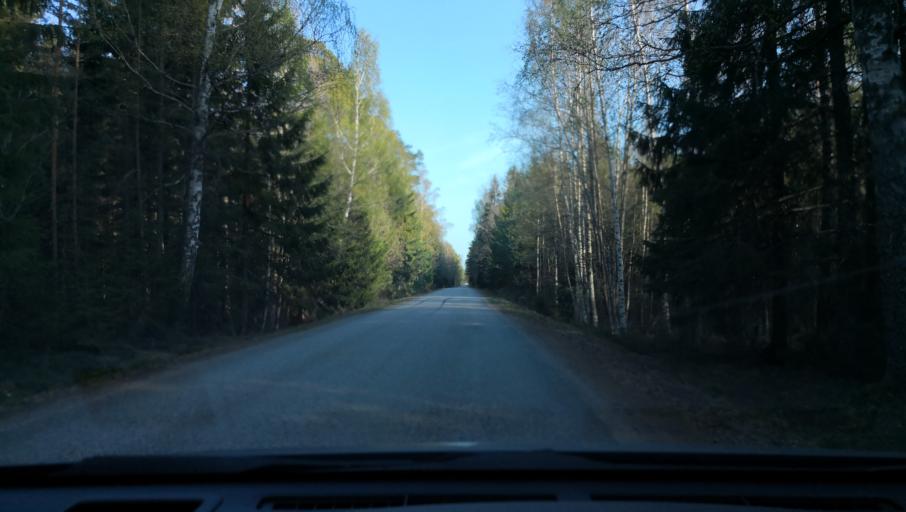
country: SE
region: Uppsala
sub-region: Heby Kommun
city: Tarnsjo
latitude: 60.2753
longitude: 16.8984
